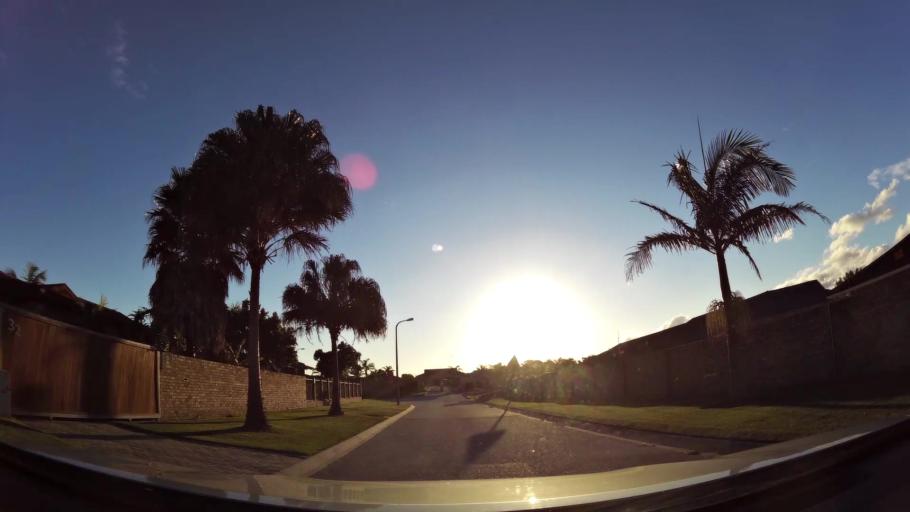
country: ZA
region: Eastern Cape
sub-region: Nelson Mandela Bay Metropolitan Municipality
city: Port Elizabeth
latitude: -33.9659
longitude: 25.4851
